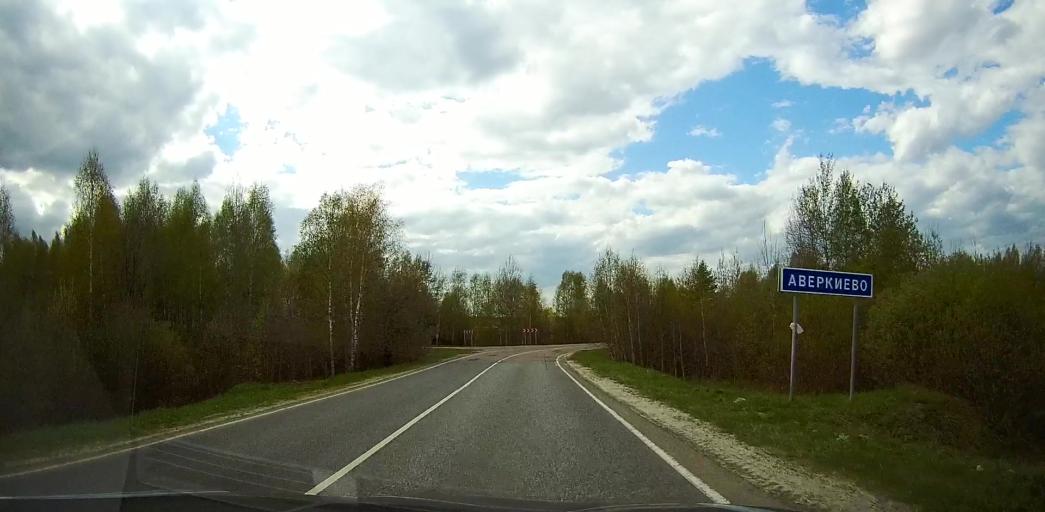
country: RU
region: Moskovskaya
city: Rakhmanovo
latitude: 55.6528
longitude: 38.6406
